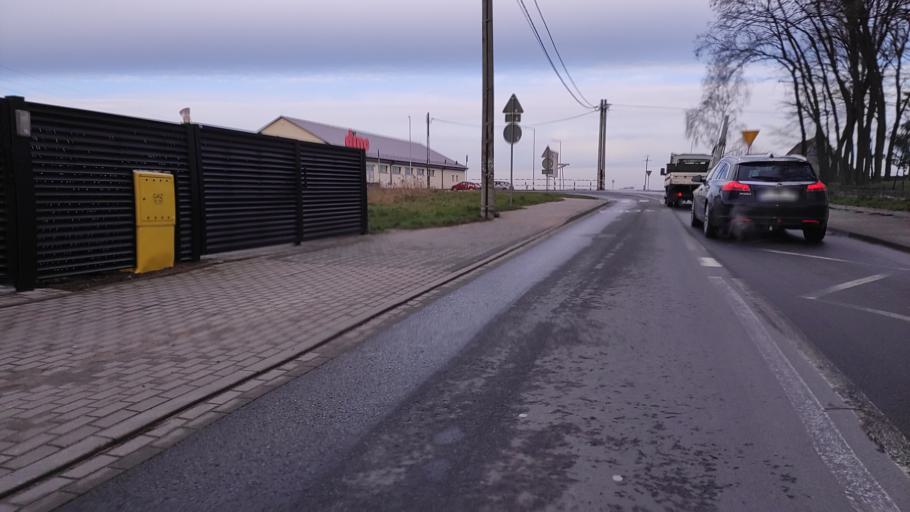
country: PL
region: Greater Poland Voivodeship
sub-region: Powiat poznanski
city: Kostrzyn
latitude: 52.4020
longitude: 17.1599
